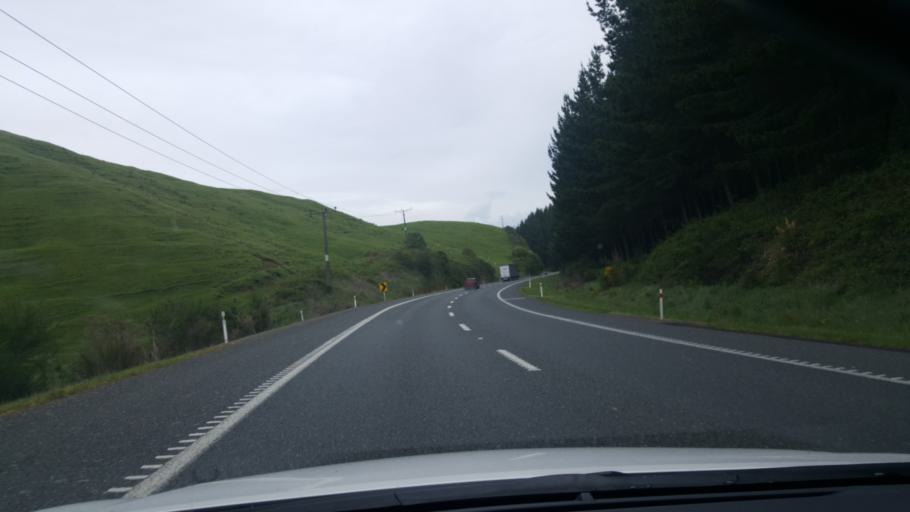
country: NZ
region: Bay of Plenty
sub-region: Rotorua District
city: Rotorua
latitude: -38.2823
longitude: 176.3466
